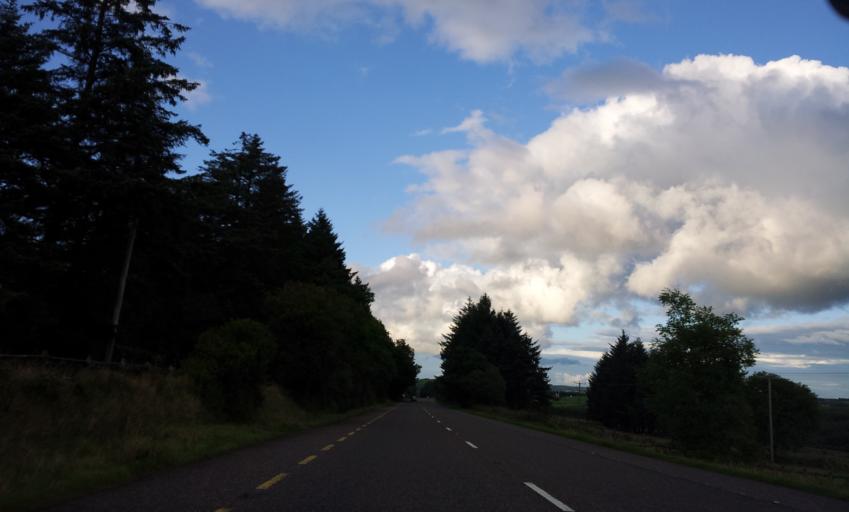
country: IE
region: Munster
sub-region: Ciarrai
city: Castleisland
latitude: 52.2919
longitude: -9.3974
